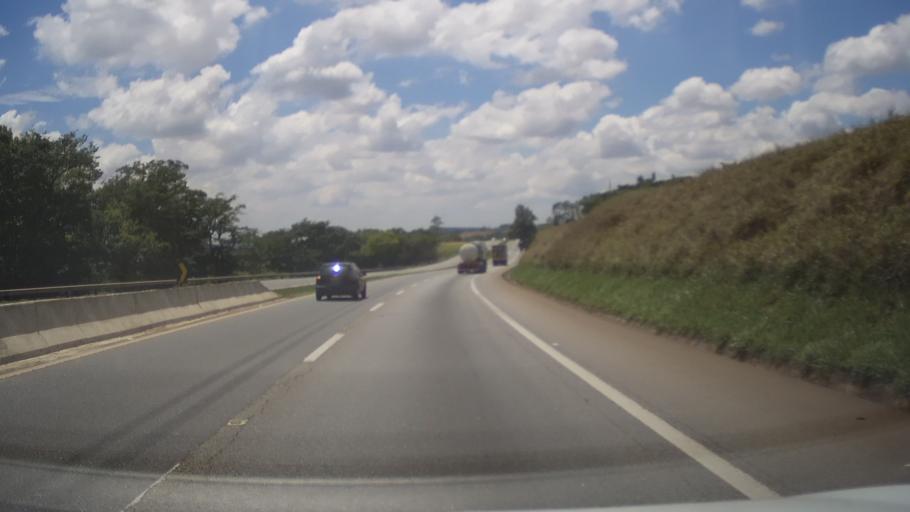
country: BR
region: Minas Gerais
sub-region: Campanha
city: Campanha
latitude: -21.8014
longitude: -45.4698
